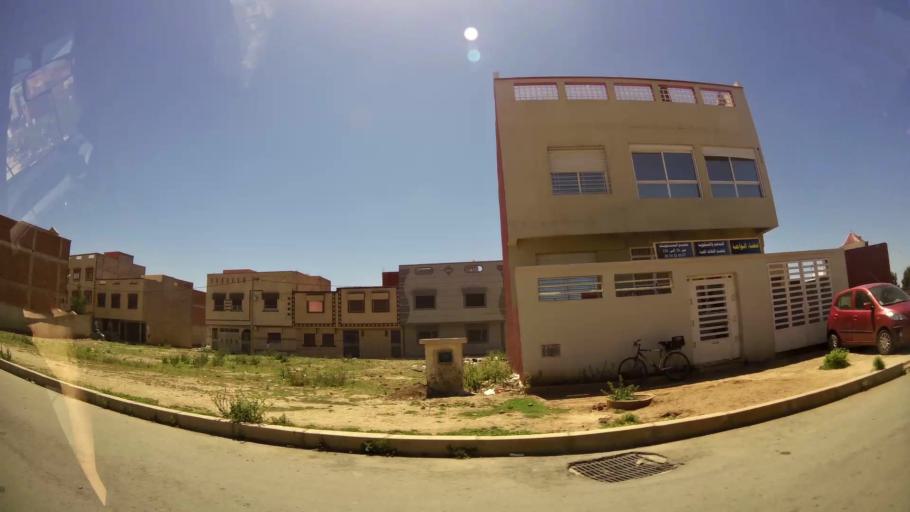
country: MA
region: Oriental
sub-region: Oujda-Angad
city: Oujda
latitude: 34.6748
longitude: -1.8666
